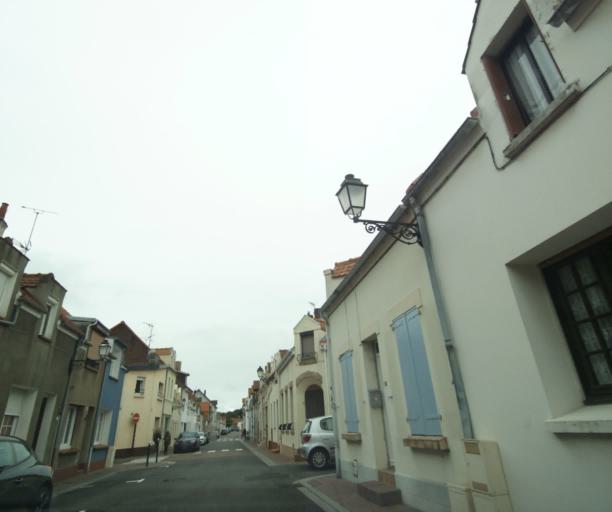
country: FR
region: Nord-Pas-de-Calais
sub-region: Departement du Pas-de-Calais
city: Etaples
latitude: 50.5171
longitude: 1.6335
